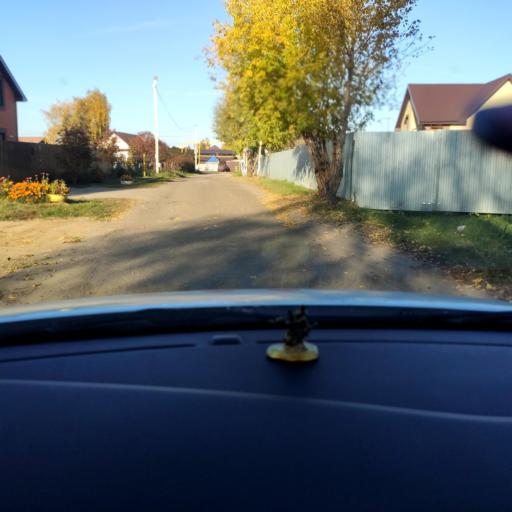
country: RU
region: Tatarstan
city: Stolbishchi
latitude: 55.6244
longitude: 49.1505
